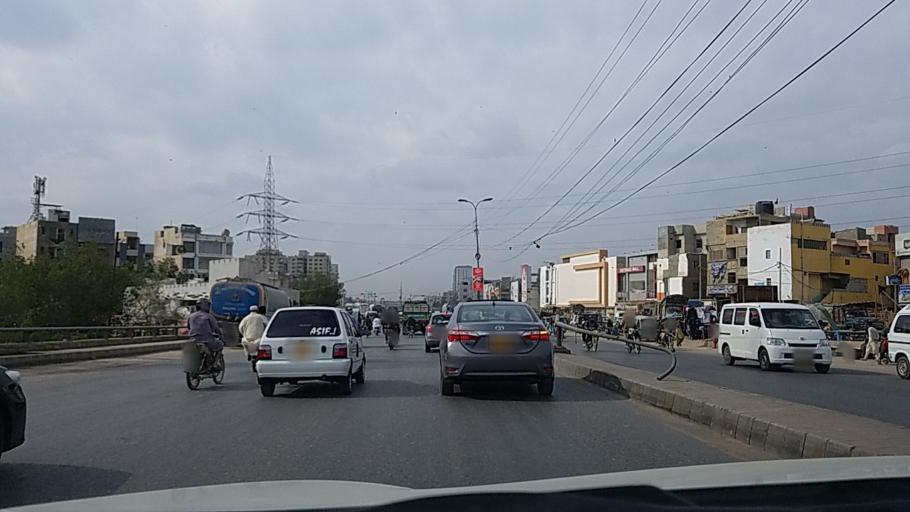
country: PK
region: Sindh
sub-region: Karachi District
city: Karachi
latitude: 24.8327
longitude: 67.0759
